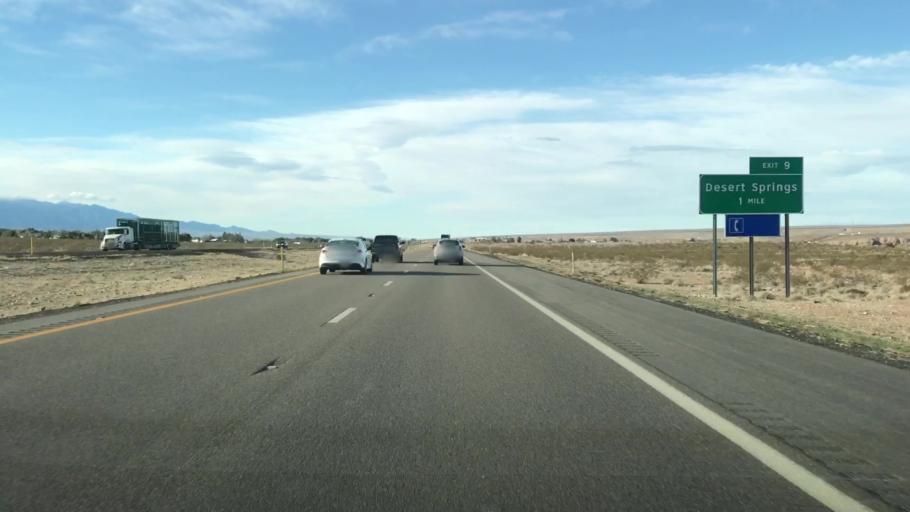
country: US
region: Arizona
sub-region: Mohave County
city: Beaver Dam
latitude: 36.9112
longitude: -113.8880
